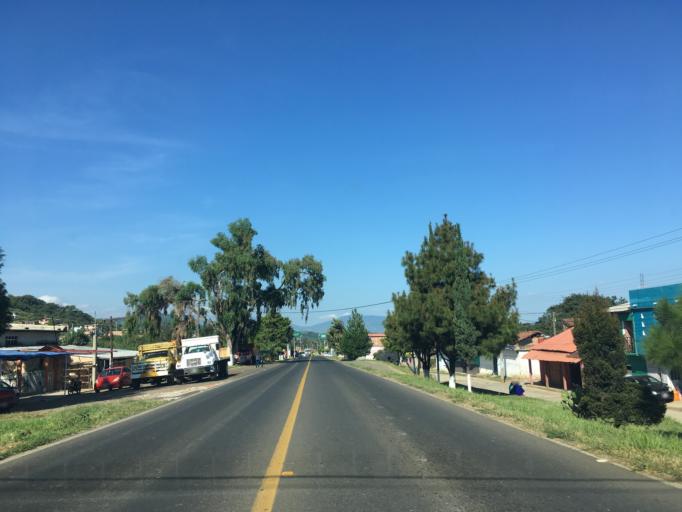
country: MX
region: Mexico
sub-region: Chalco
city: Santo Tomas
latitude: 19.8448
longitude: -102.0939
